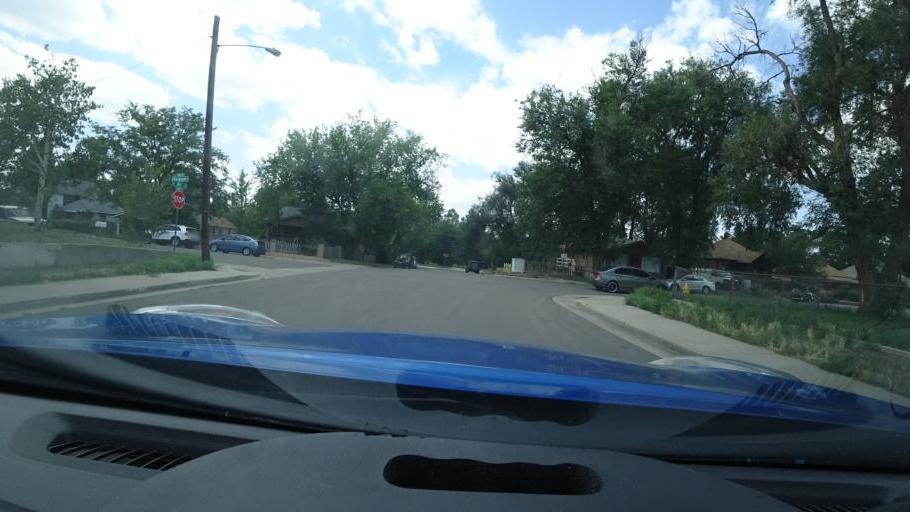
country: US
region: Colorado
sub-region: Arapahoe County
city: Englewood
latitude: 39.6747
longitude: -104.9957
